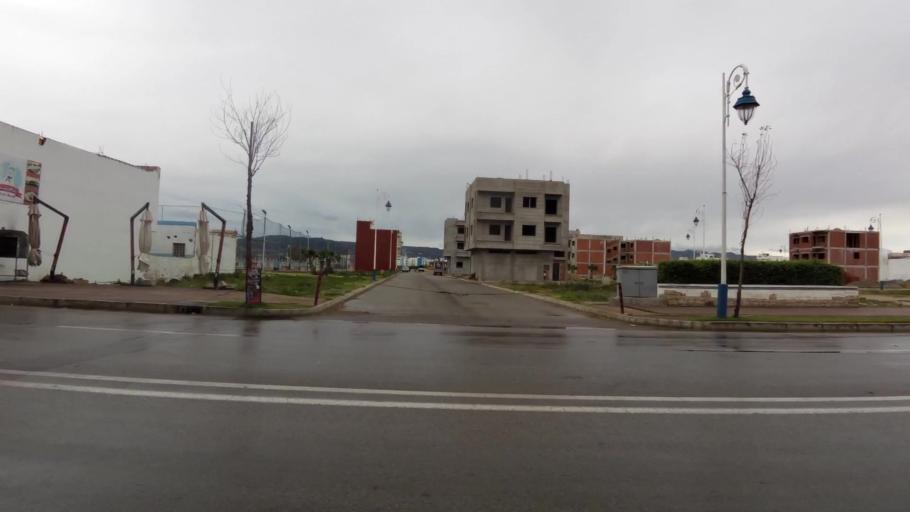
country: MA
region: Tanger-Tetouan
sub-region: Tetouan
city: Martil
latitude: 35.6257
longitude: -5.2917
